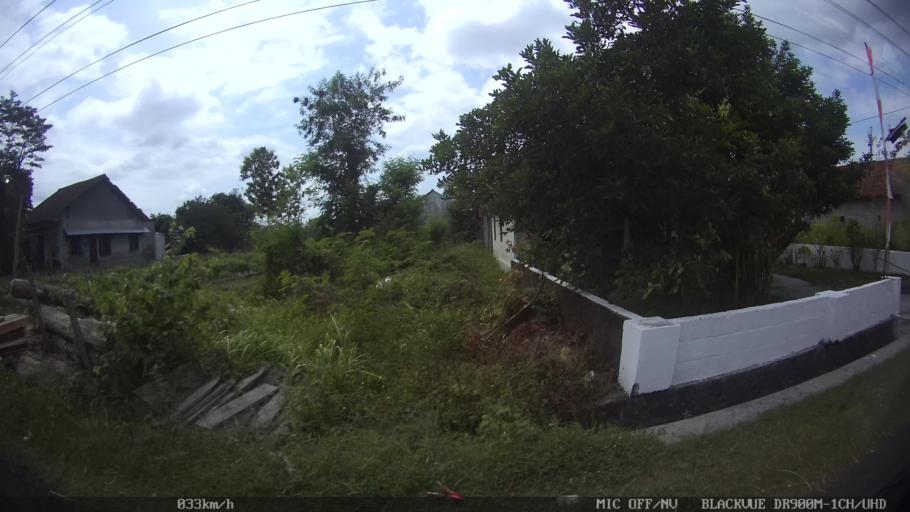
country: ID
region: Daerah Istimewa Yogyakarta
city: Depok
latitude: -7.7862
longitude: 110.4638
